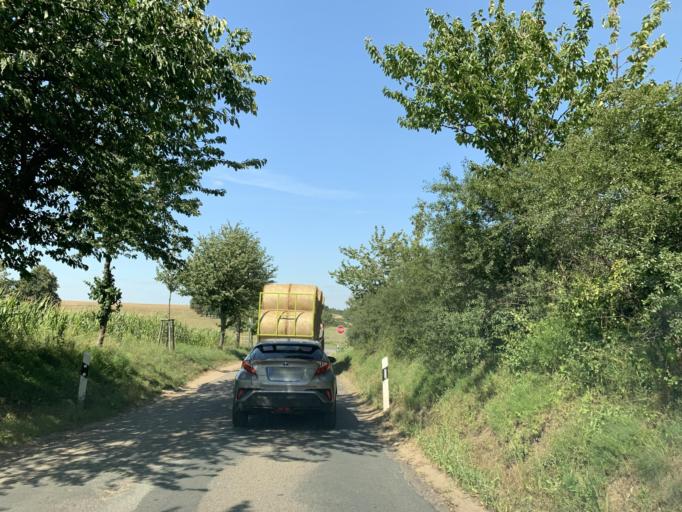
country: DE
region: Mecklenburg-Vorpommern
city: Loitz
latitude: 53.3633
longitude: 13.3863
